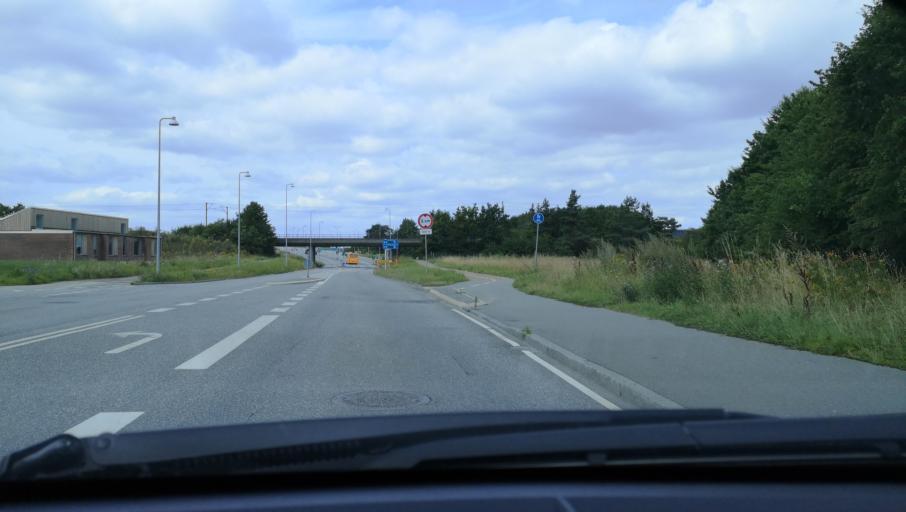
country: DK
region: Zealand
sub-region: Solrod Kommune
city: Solrod
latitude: 55.5030
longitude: 12.1838
